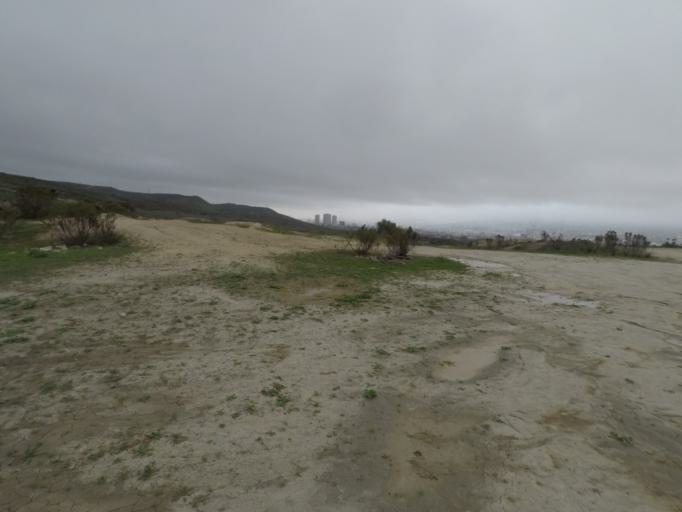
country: MX
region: Baja California
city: Tijuana
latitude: 32.5562
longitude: -117.0369
